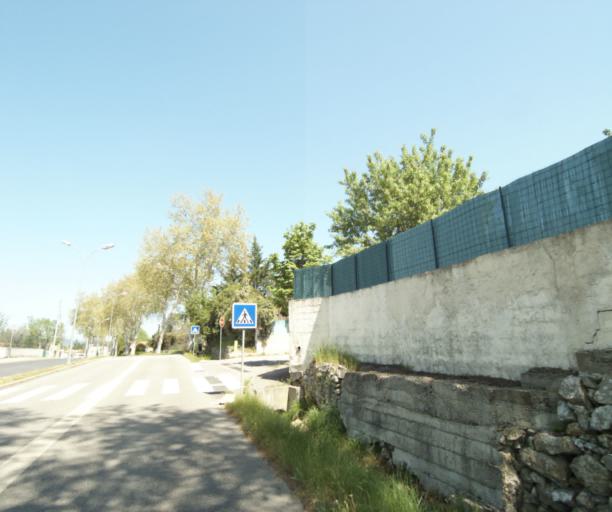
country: FR
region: Languedoc-Roussillon
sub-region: Departement de l'Herault
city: Prades-le-Lez
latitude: 43.6915
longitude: 3.8628
